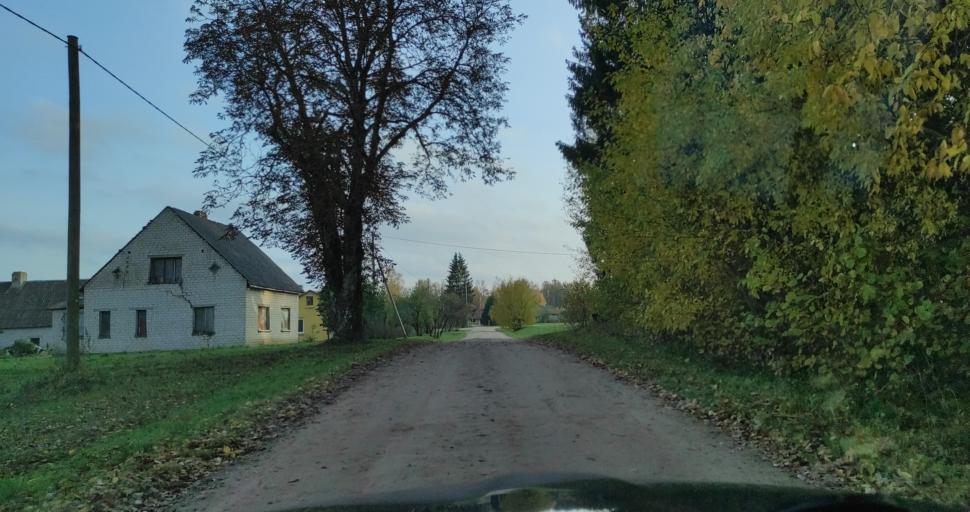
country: LV
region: Vainode
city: Vainode
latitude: 56.4239
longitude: 21.8743
